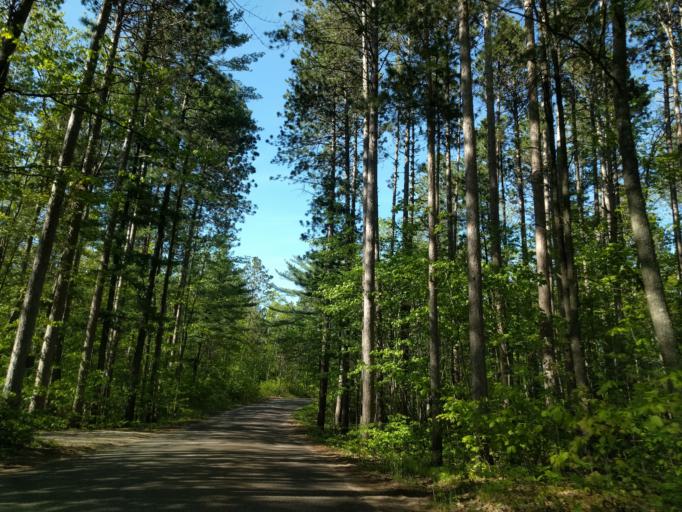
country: US
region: Michigan
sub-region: Marquette County
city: Gwinn
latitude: 46.2744
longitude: -87.3691
